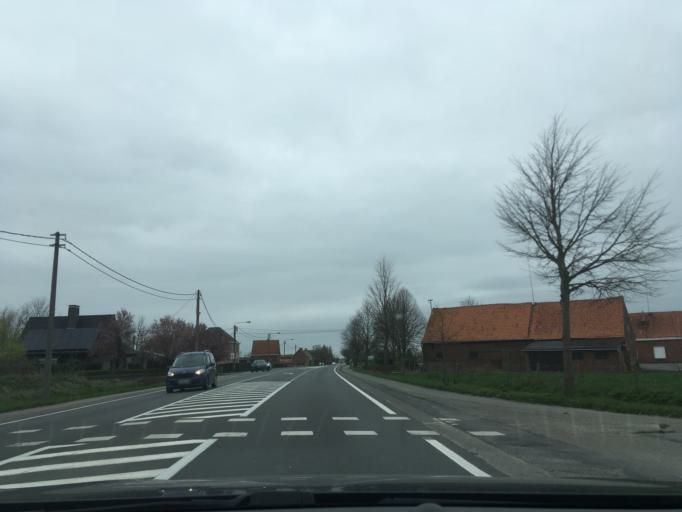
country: BE
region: Flanders
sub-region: Provincie West-Vlaanderen
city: Torhout
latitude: 51.0237
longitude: 3.1056
